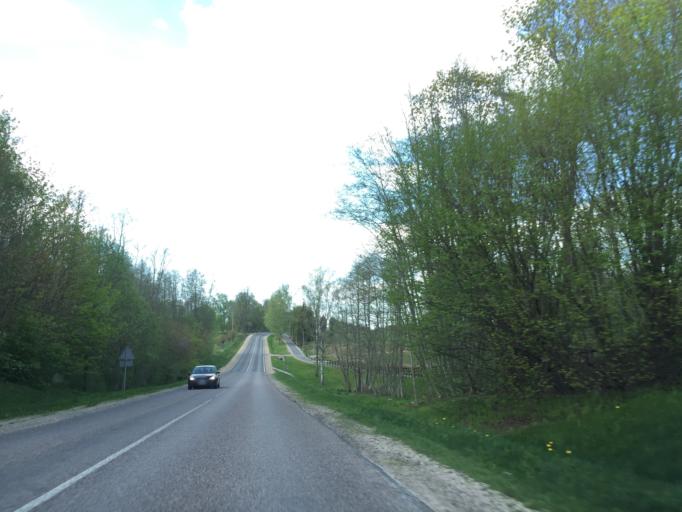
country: LV
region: Limbazu Rajons
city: Limbazi
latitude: 57.4879
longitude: 24.7097
